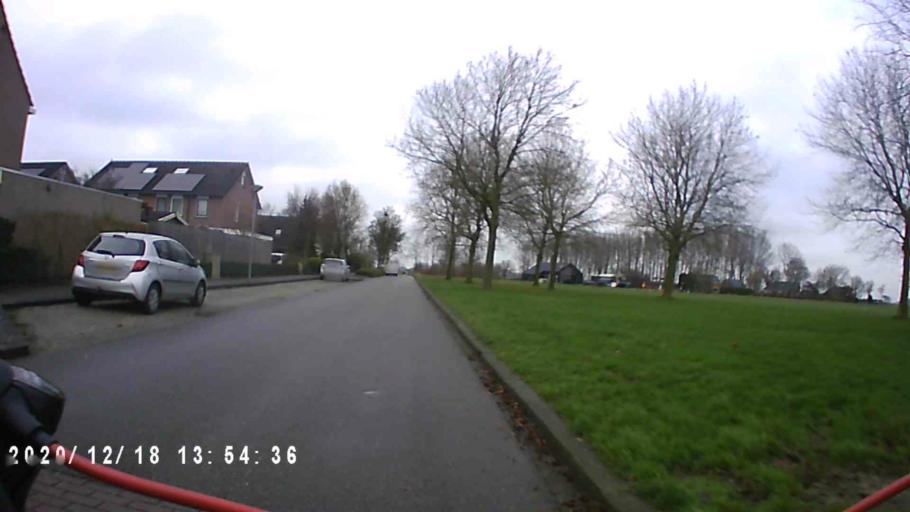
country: NL
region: Groningen
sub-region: Gemeente Bedum
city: Bedum
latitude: 53.3002
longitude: 6.6141
